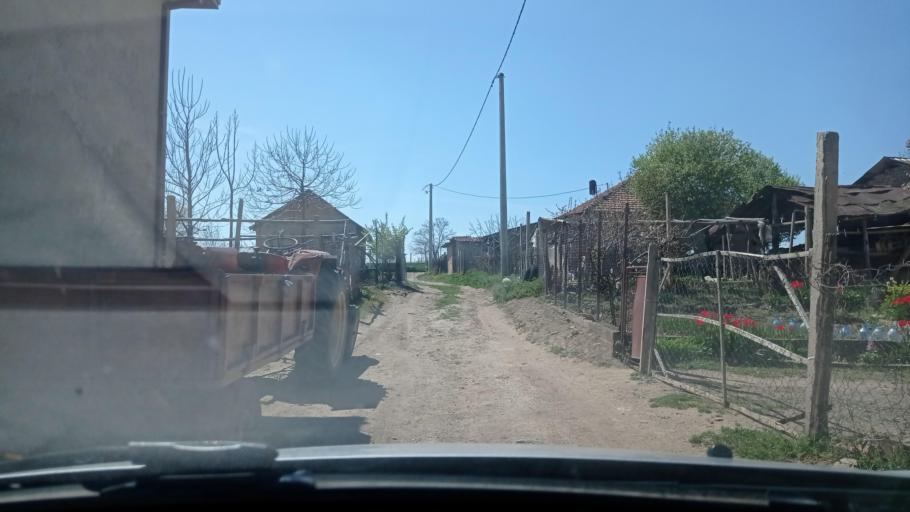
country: MK
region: Lozovo
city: Lozovo
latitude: 41.7626
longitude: 21.8653
